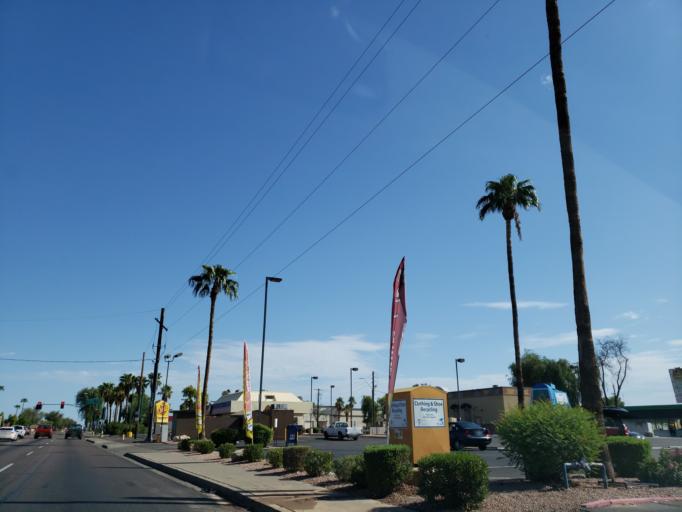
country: US
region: Arizona
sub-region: Maricopa County
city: Glendale
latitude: 33.4937
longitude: -112.2205
